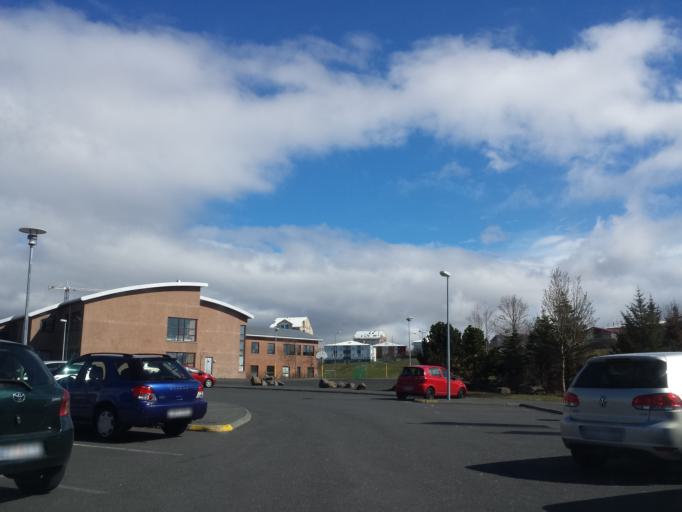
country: IS
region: Capital Region
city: Kopavogur
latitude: 64.1030
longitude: -21.8976
